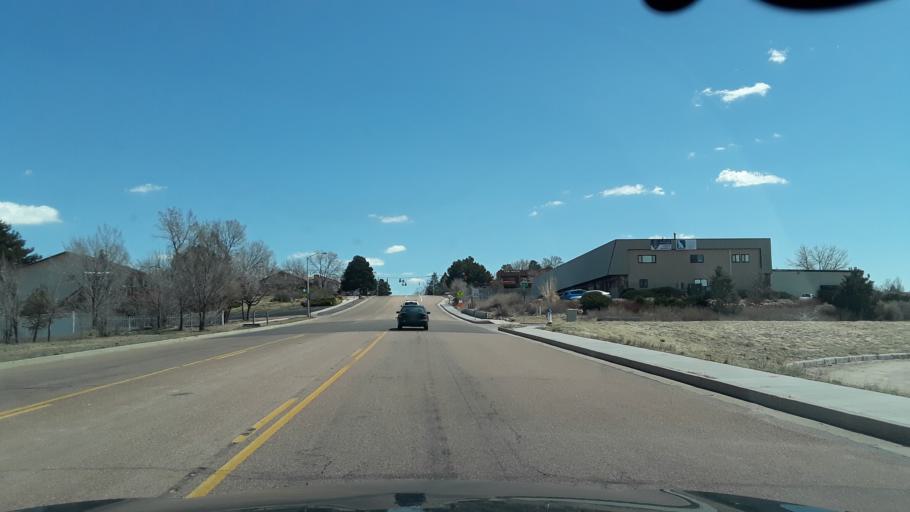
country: US
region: Colorado
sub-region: El Paso County
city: Cimarron Hills
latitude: 38.8462
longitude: -104.7113
